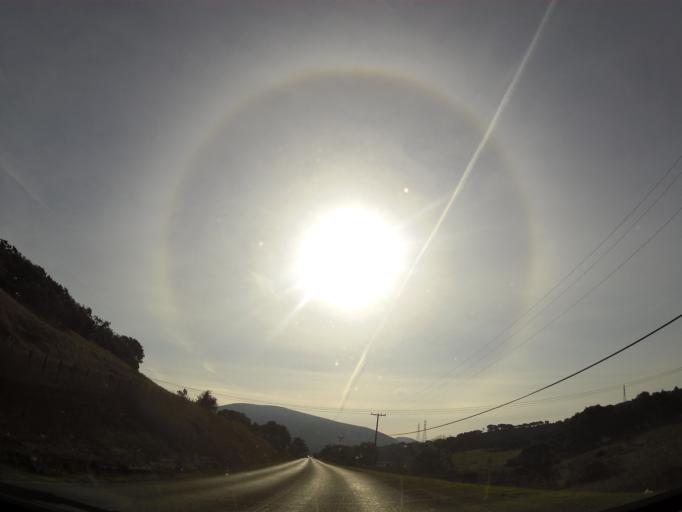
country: US
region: California
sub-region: Monterey County
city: Prunedale
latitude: 36.7842
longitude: -121.6110
